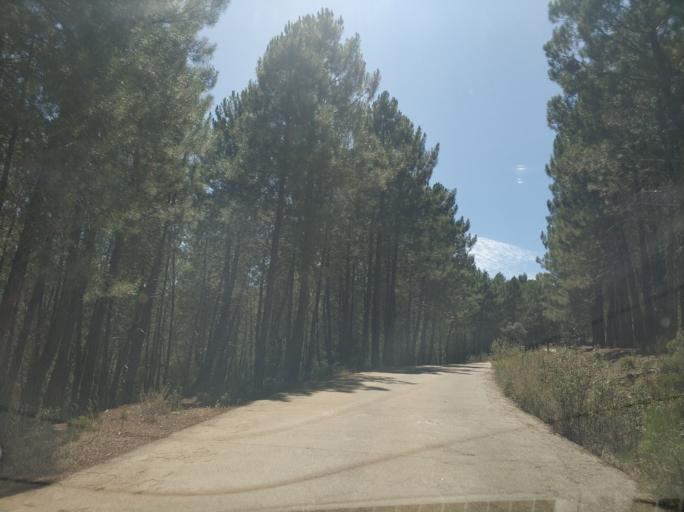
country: ES
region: Castille and Leon
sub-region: Provincia de Salamanca
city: Herguijuela de la Sierra
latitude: 40.3978
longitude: -6.0755
